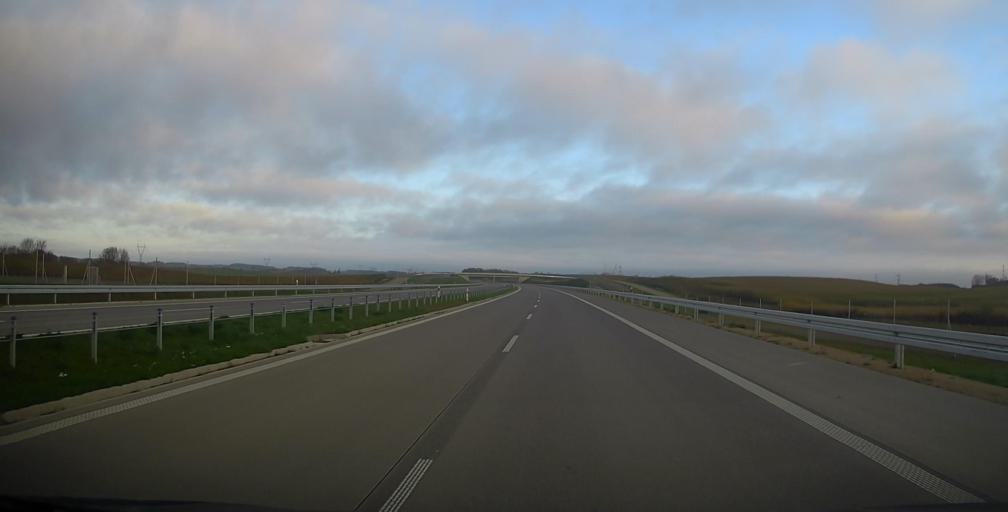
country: PL
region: Podlasie
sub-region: Powiat grajewski
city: Szczuczyn
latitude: 53.6548
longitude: 22.2978
